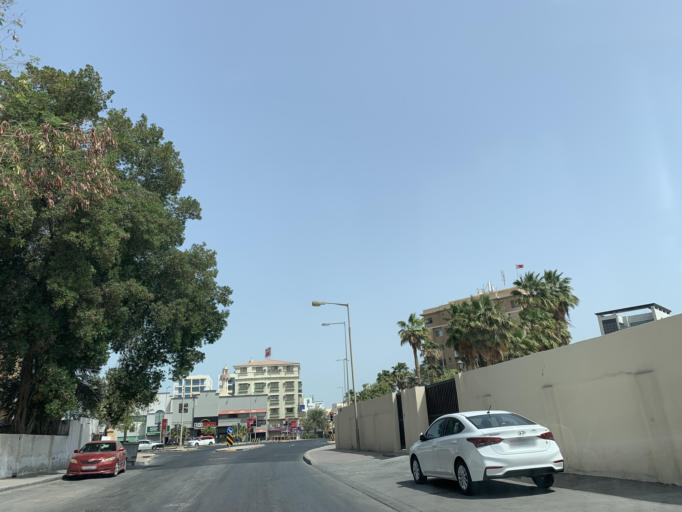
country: BH
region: Manama
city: Manama
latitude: 26.2113
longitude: 50.5858
